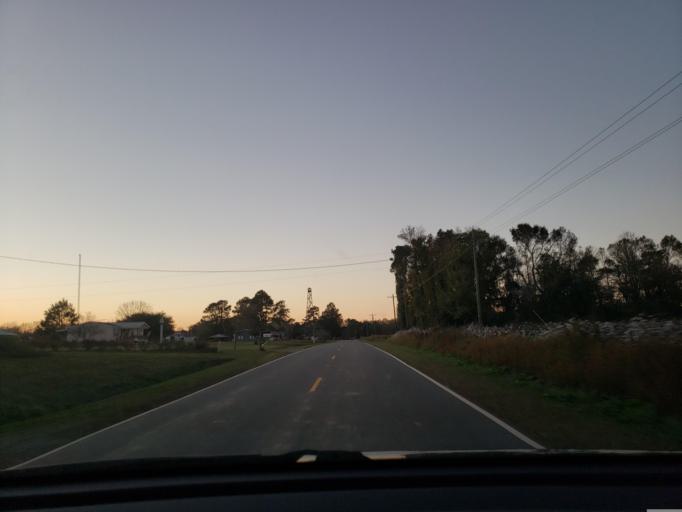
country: US
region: North Carolina
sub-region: Duplin County
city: Beulaville
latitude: 34.7900
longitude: -77.7616
